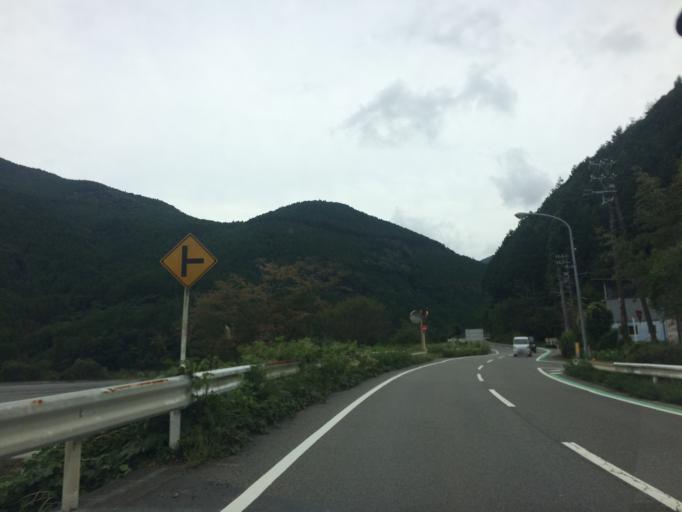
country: JP
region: Shizuoka
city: Kanaya
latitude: 35.0334
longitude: 138.0837
